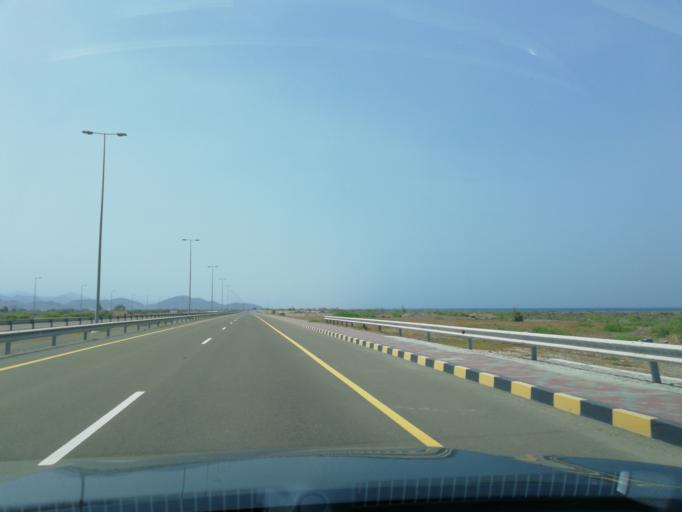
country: OM
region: Al Batinah
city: Shinas
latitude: 24.9073
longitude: 56.3935
